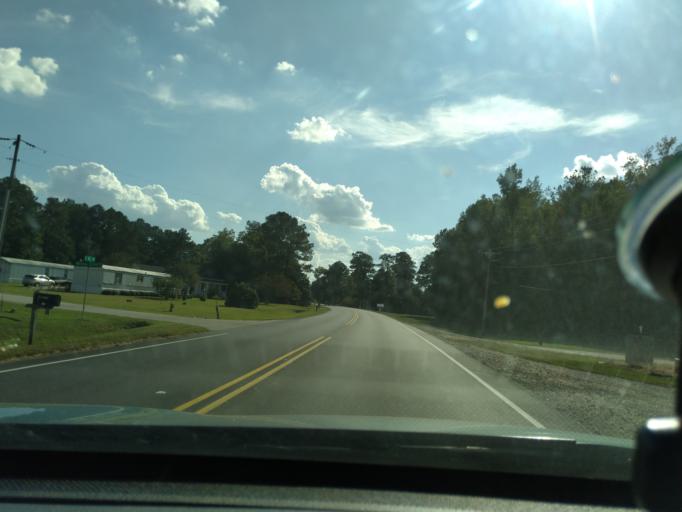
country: US
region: North Carolina
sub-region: Nash County
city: Sharpsburg
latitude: 35.9046
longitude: -77.8491
